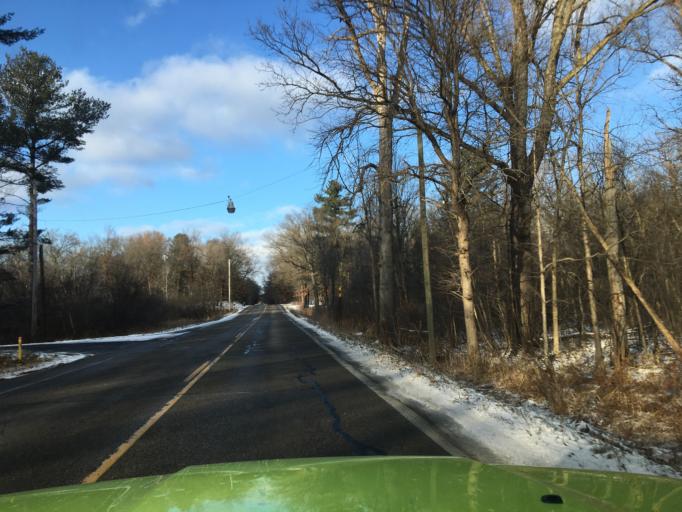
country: US
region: Michigan
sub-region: Montcalm County
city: Greenville
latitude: 43.1927
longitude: -85.2829
